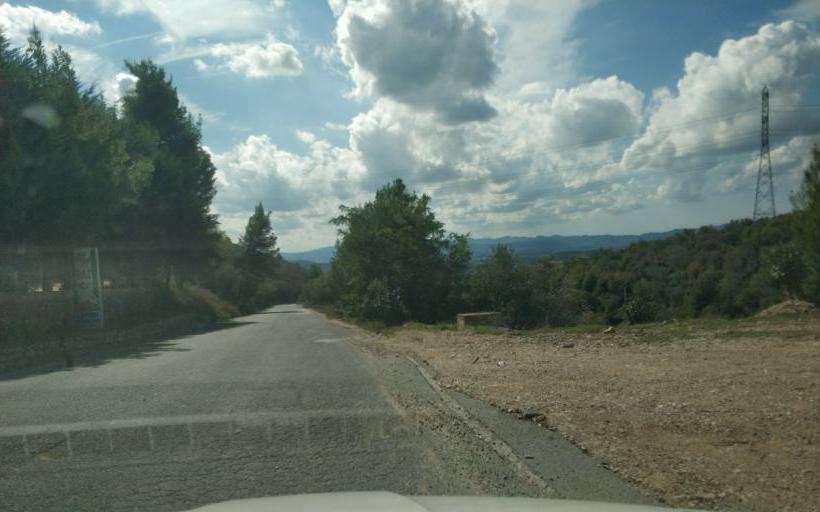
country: AL
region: Durres
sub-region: Rrethi i Krujes
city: Kruje
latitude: 41.4874
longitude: 19.7674
